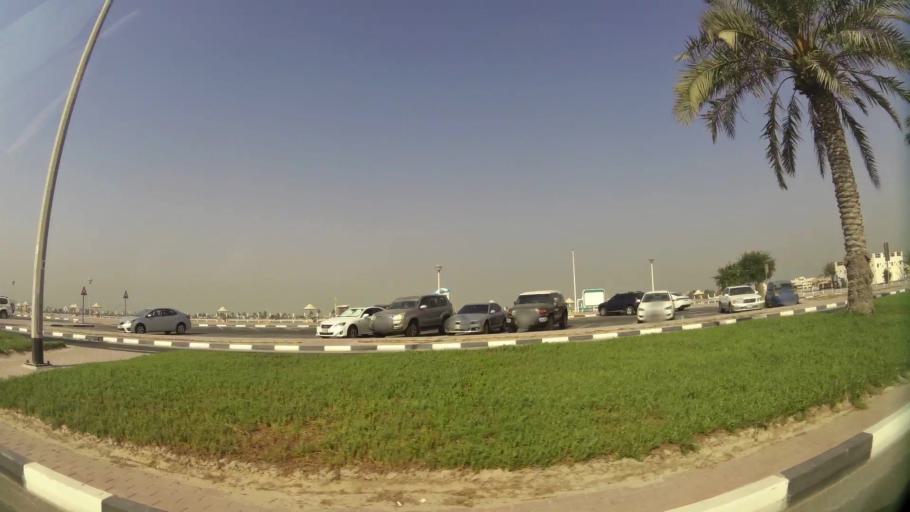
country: AE
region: Ash Shariqah
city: Sharjah
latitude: 25.3089
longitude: 55.3524
